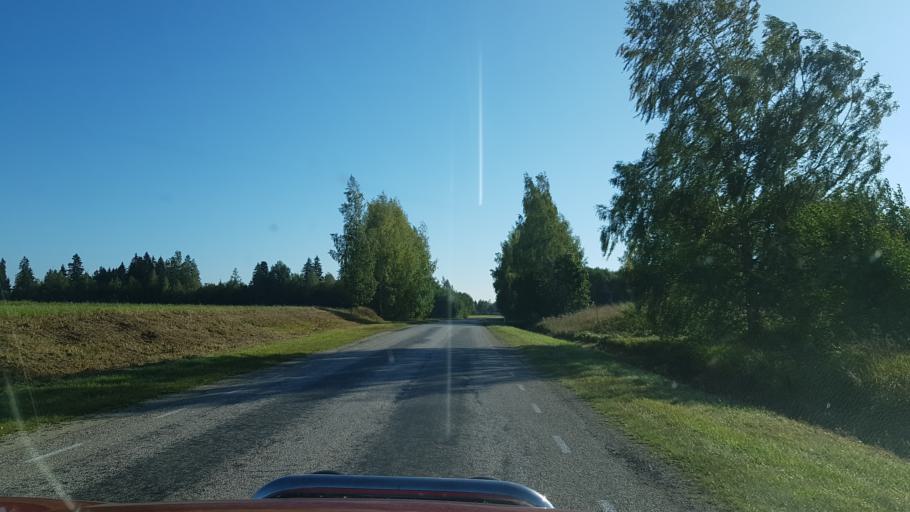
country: EE
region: Jogevamaa
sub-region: Tabivere vald
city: Tabivere
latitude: 58.6803
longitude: 26.6383
